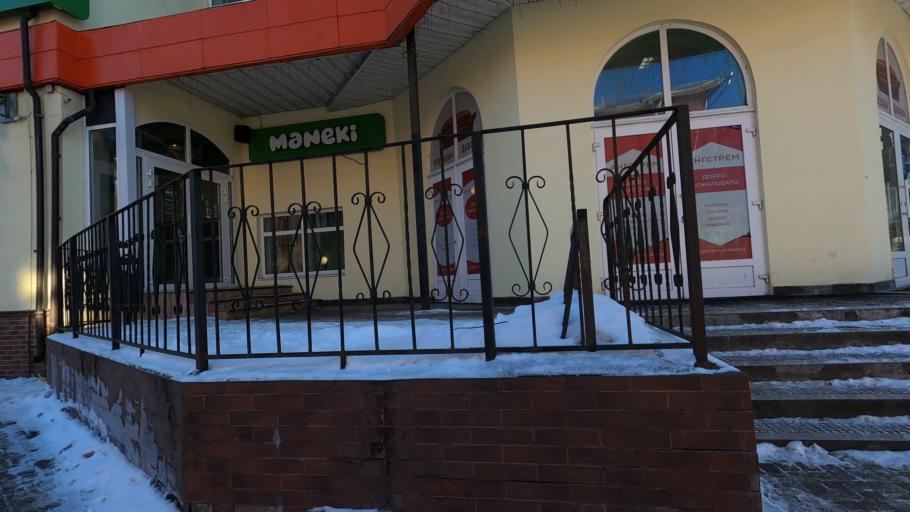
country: RU
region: Jaroslavl
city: Rybinsk
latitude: 58.0483
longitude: 38.8401
